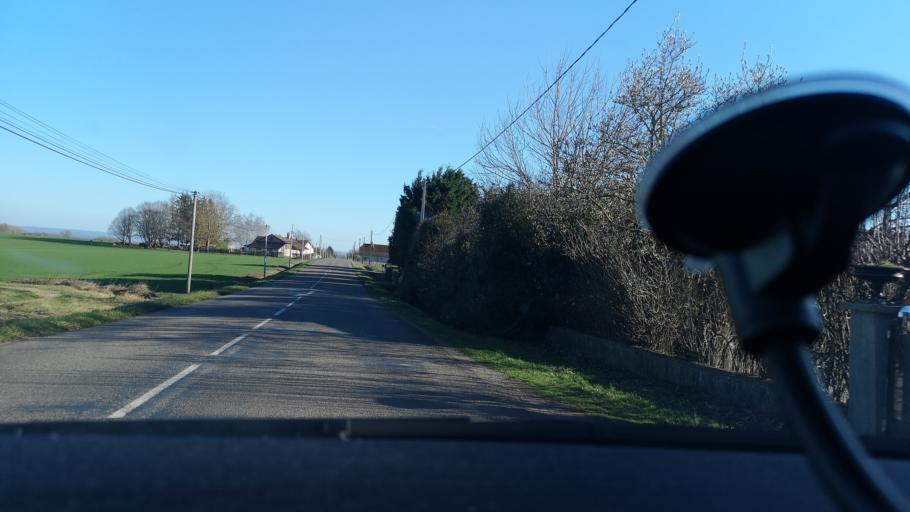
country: FR
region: Bourgogne
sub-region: Departement de Saone-et-Loire
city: Saint-Germain-du-Bois
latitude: 46.7451
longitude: 5.3430
